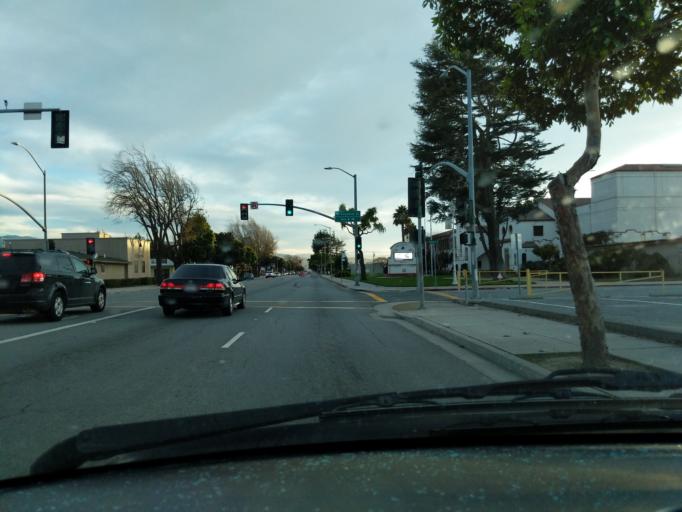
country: US
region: California
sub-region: Monterey County
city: Salinas
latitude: 36.6680
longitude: -121.6560
